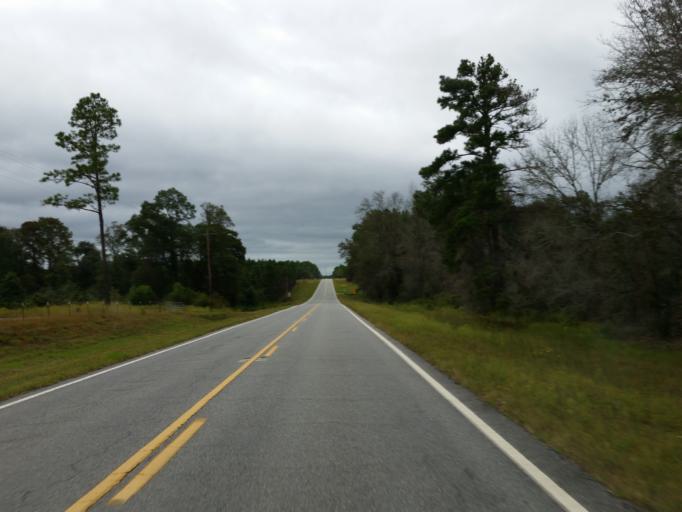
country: US
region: Georgia
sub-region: Lanier County
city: Lakeland
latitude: 30.8950
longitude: -83.0053
